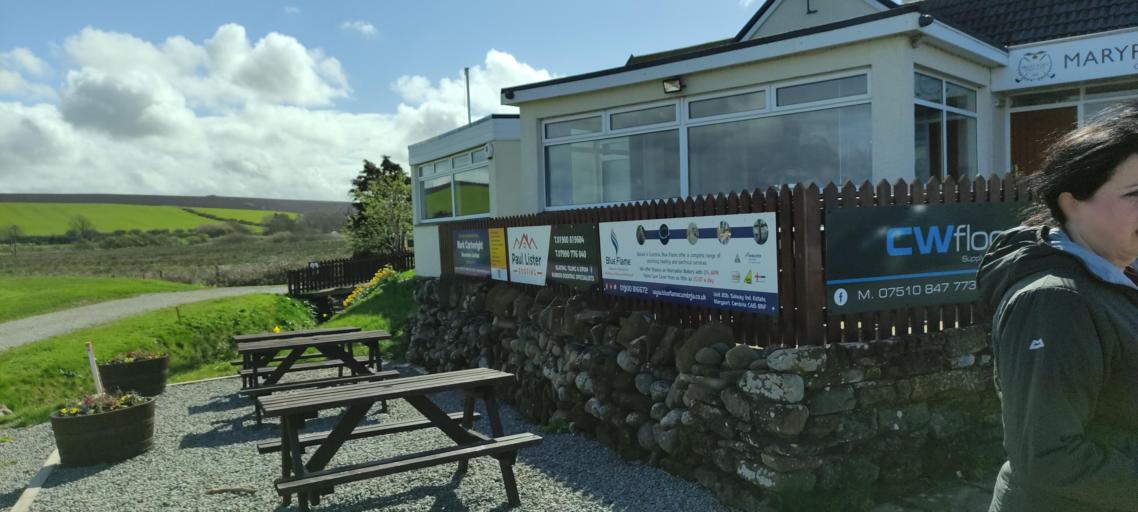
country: GB
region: England
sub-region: Cumbria
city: Maryport
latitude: 54.7315
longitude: -3.4783
